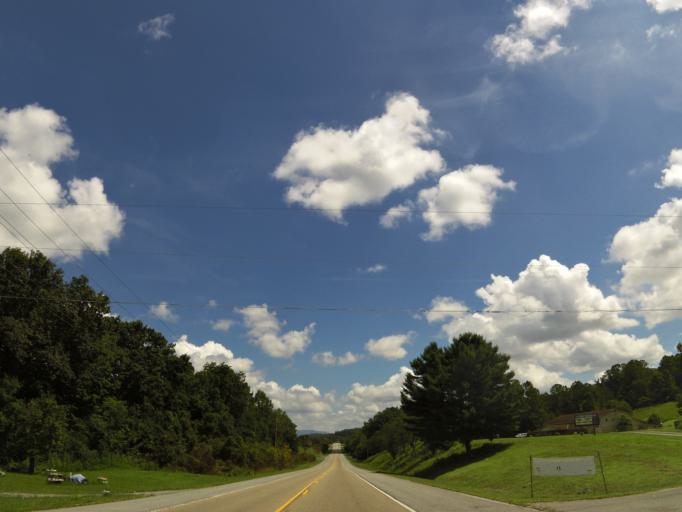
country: US
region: Tennessee
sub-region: Claiborne County
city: Harrogate
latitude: 36.5408
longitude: -83.6818
